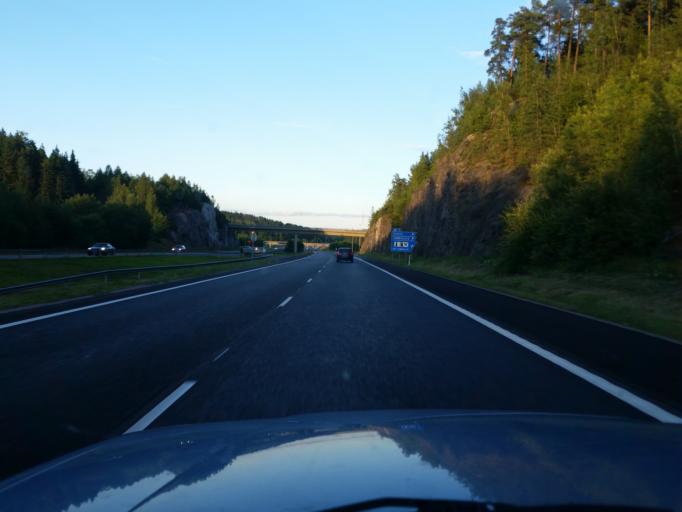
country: FI
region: Varsinais-Suomi
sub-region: Turku
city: Piikkioe
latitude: 60.4427
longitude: 22.5881
